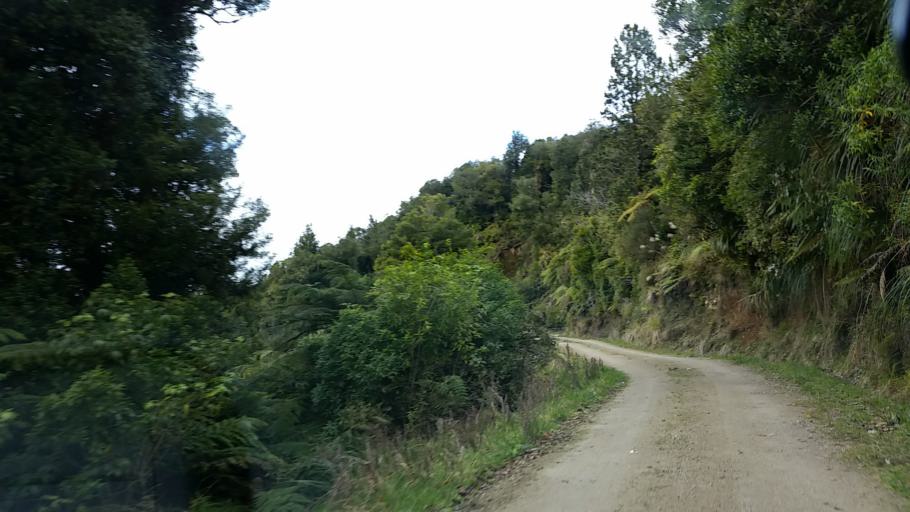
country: NZ
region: Taranaki
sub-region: South Taranaki District
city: Patea
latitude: -39.5835
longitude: 174.6809
